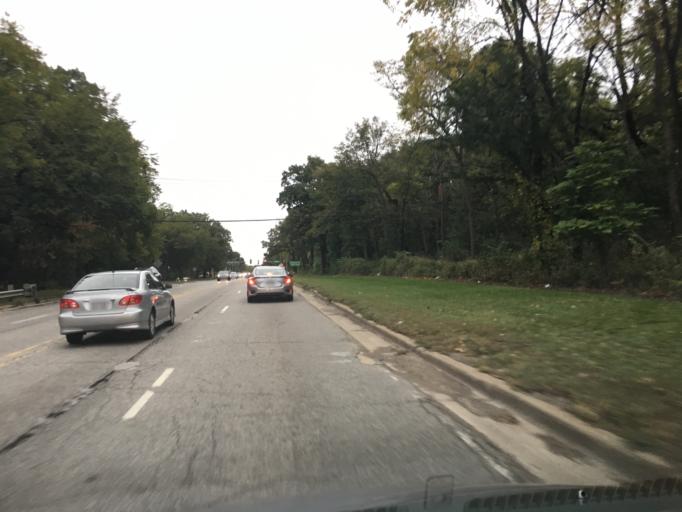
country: US
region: Illinois
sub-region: Cook County
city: Riverside
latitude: 41.8254
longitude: -87.8287
